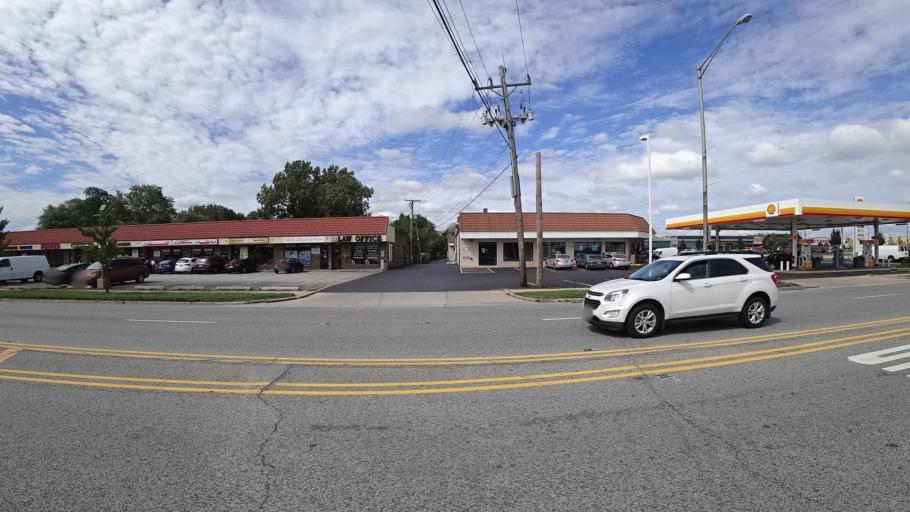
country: US
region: Illinois
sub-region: Cook County
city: Worth
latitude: 41.7036
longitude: -87.7980
